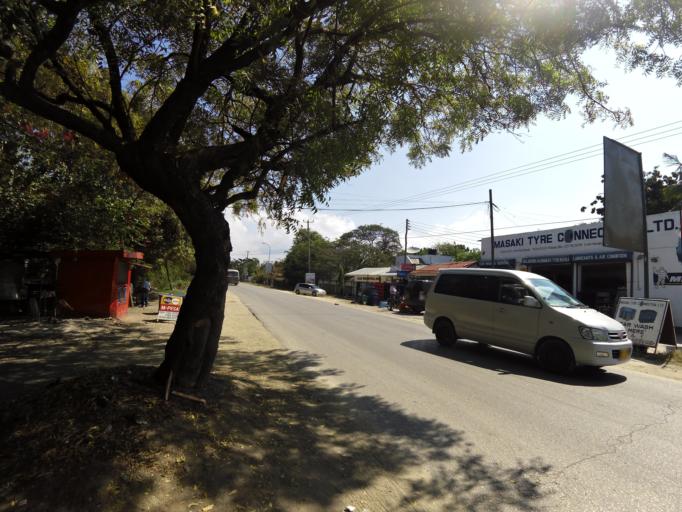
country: TZ
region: Dar es Salaam
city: Magomeni
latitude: -6.7469
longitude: 39.2759
